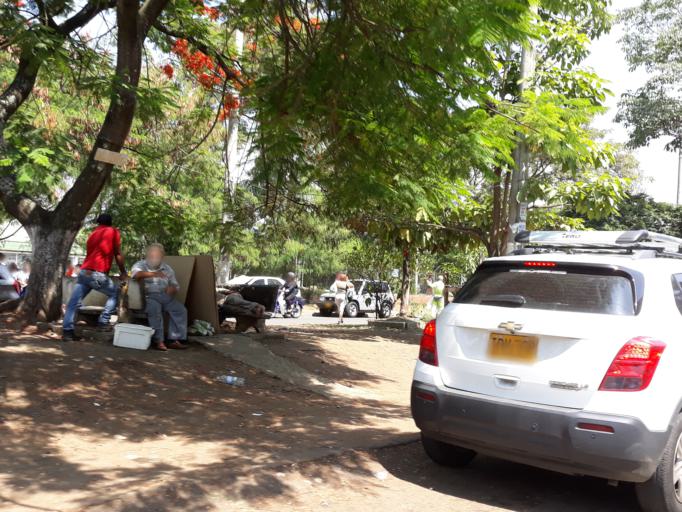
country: CO
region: Valle del Cauca
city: Cali
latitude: 3.4704
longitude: -76.4920
